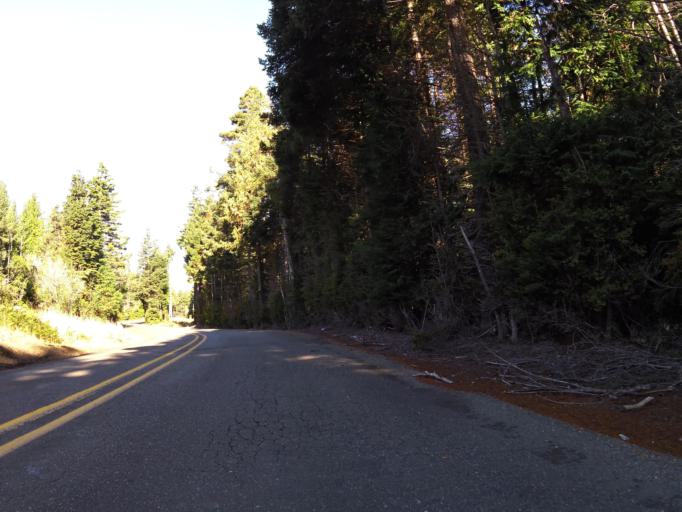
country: US
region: Oregon
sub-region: Coos County
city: Bandon
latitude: 43.0373
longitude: -124.3945
